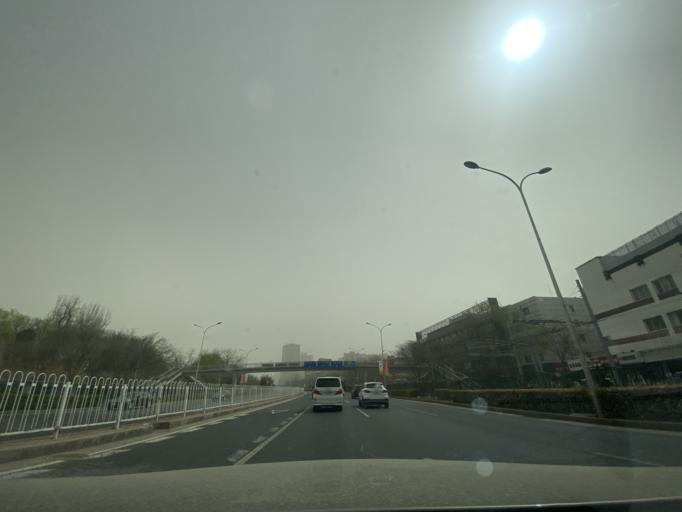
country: CN
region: Beijing
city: Sijiqing
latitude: 39.9385
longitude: 116.3103
